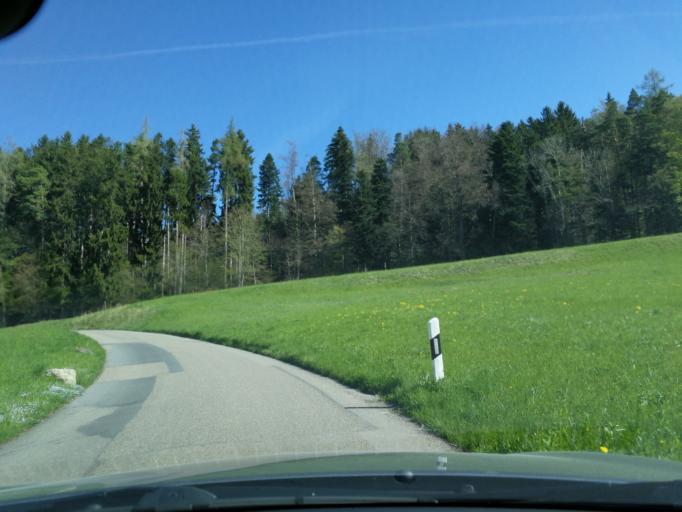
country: CH
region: Zurich
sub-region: Bezirk Meilen
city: Uetikon / Grossdorf
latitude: 47.2793
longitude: 8.6781
